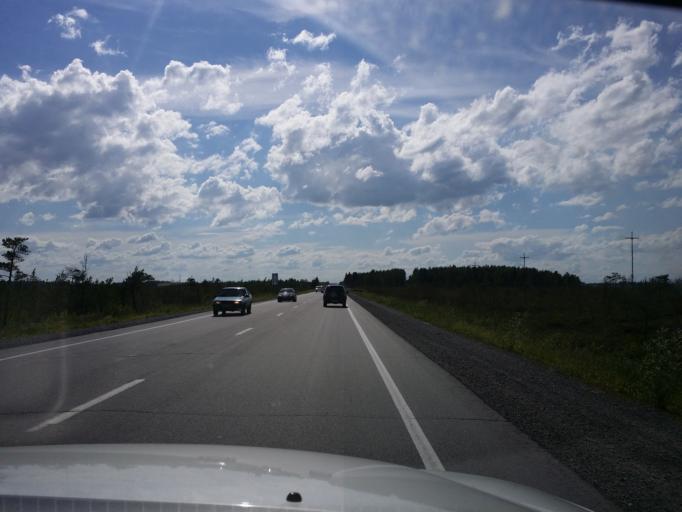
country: RU
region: Khanty-Mansiyskiy Avtonomnyy Okrug
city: Nizhnevartovsk
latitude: 60.9591
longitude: 76.7356
